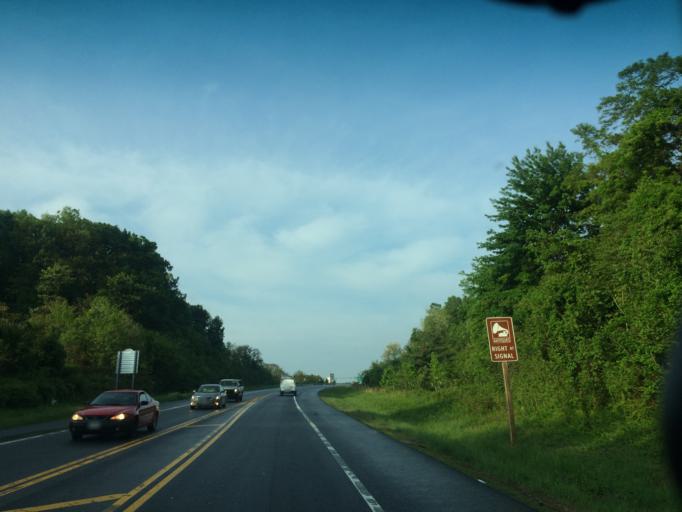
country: US
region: Maryland
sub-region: Carroll County
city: Mount Airy
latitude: 39.3719
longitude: -77.1459
